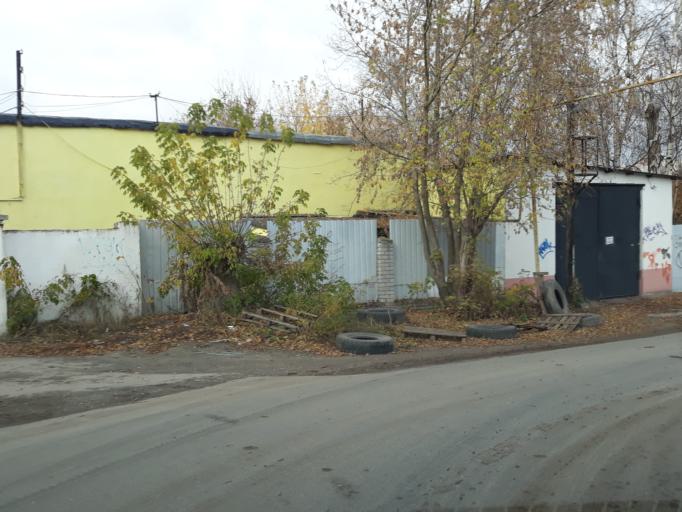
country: RU
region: Nizjnij Novgorod
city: Nizhniy Novgorod
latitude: 56.2525
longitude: 43.9766
